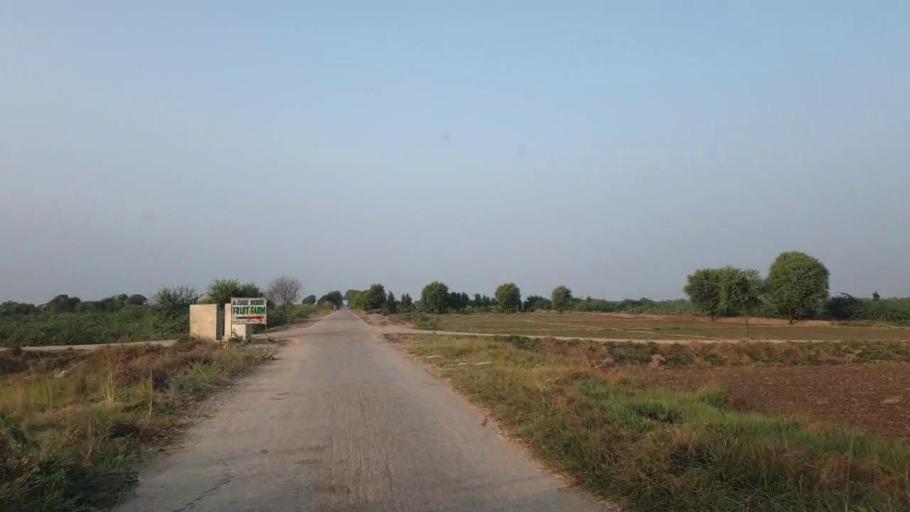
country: PK
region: Sindh
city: Tando Ghulam Ali
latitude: 25.0797
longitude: 68.9585
